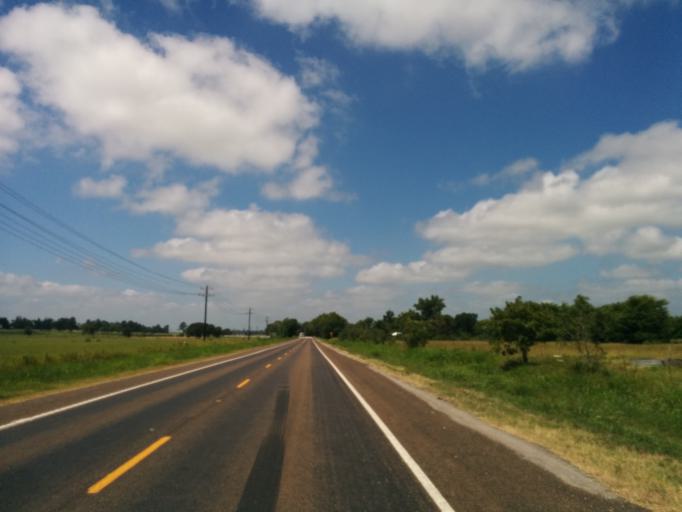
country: US
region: Texas
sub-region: Houston County
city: Crockett
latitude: 31.2890
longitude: -95.5072
